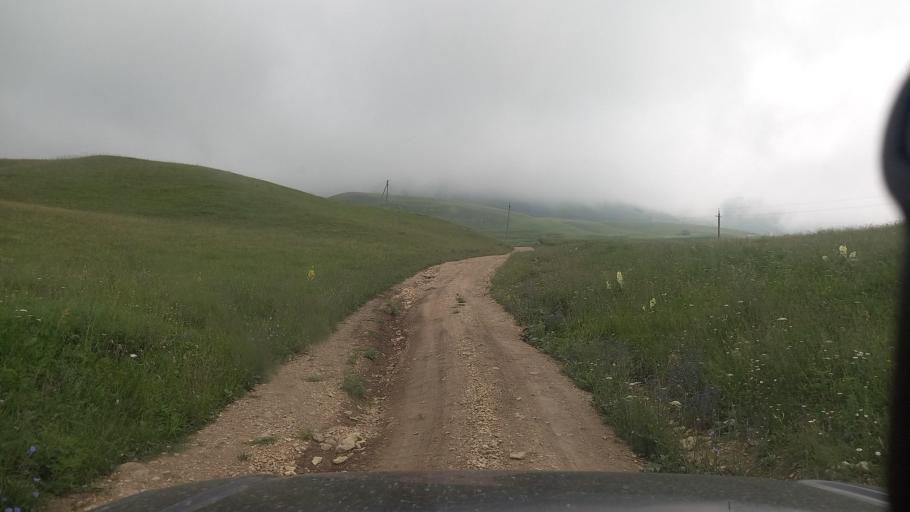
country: RU
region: Karachayevo-Cherkesiya
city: Pregradnaya
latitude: 44.0061
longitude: 41.1703
